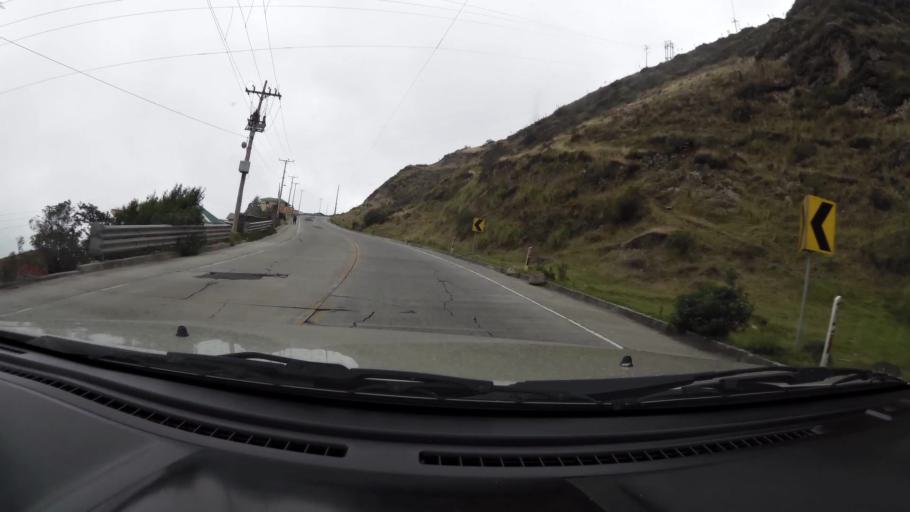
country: EC
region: Canar
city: Canar
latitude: -2.4864
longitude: -78.9950
